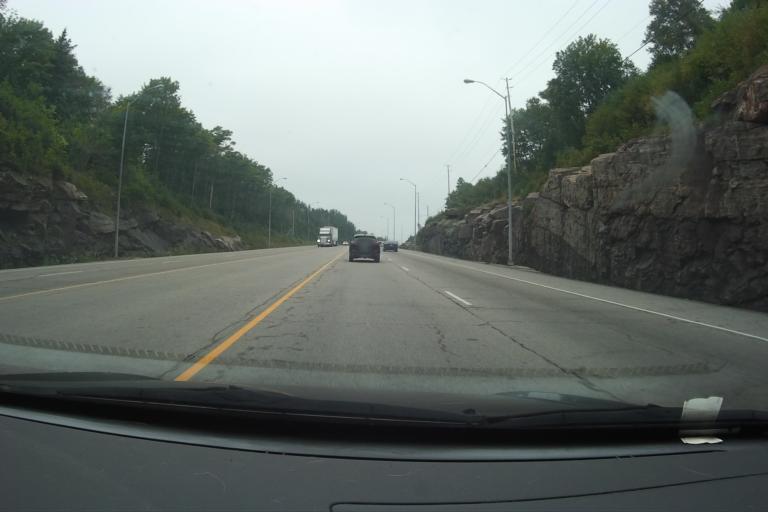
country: CA
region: Ontario
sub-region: Nipissing District
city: North Bay
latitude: 46.3424
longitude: -79.4702
